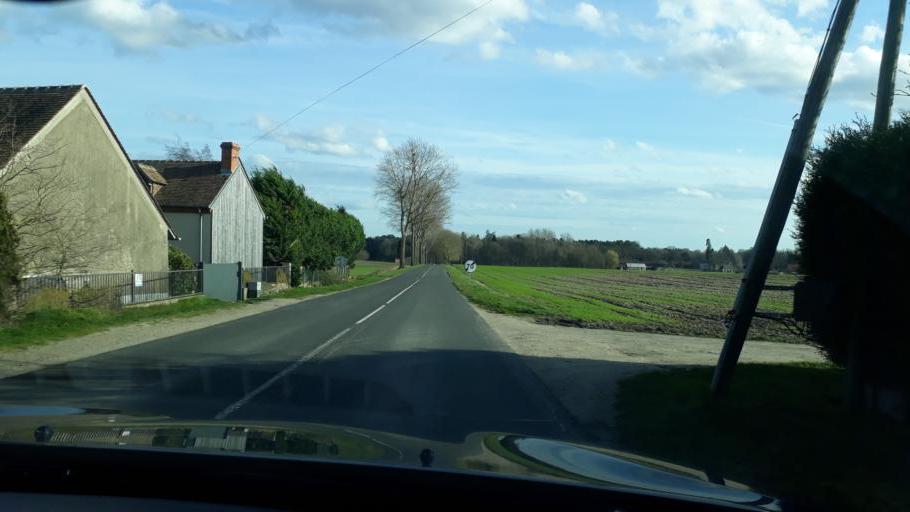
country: FR
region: Centre
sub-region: Departement du Loiret
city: Chilleurs-aux-Bois
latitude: 48.0659
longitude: 2.1482
